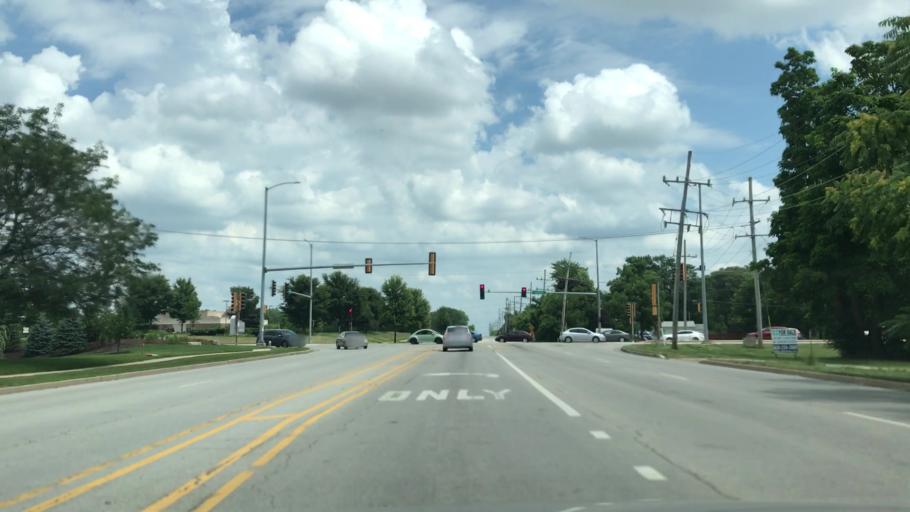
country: US
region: Illinois
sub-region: Kane County
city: Aurora
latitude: 41.7666
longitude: -88.2438
